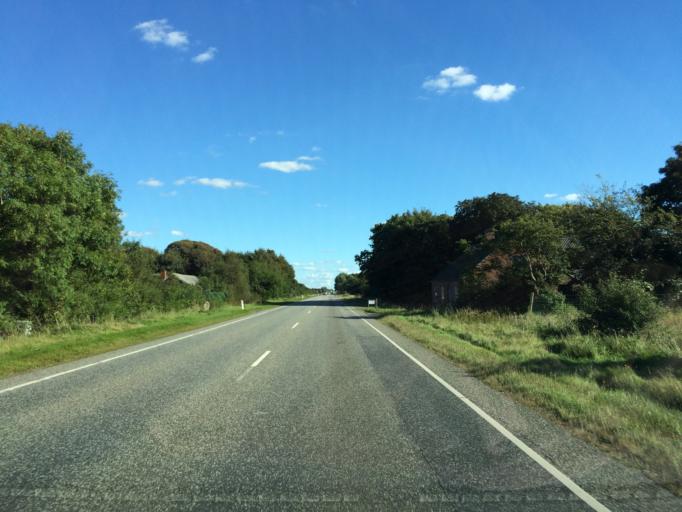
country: DK
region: Central Jutland
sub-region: Holstebro Kommune
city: Holstebro
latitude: 56.3266
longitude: 8.6648
